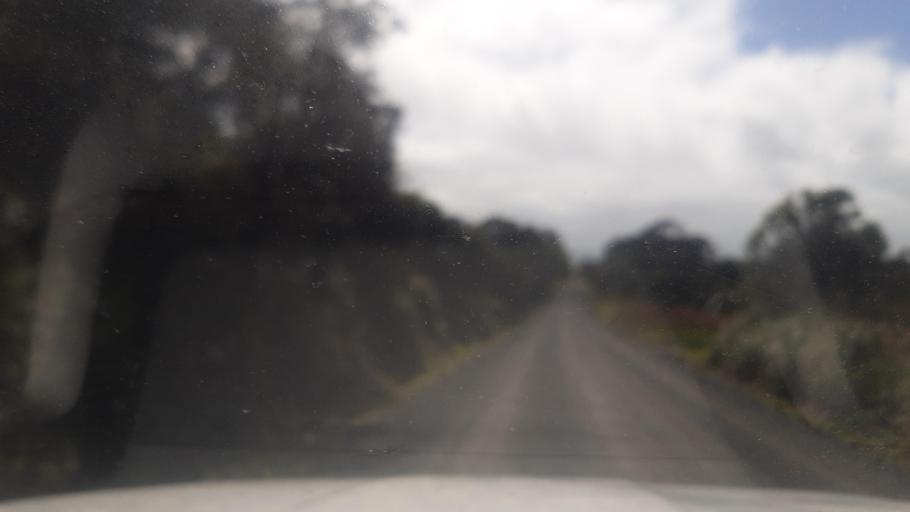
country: NZ
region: Northland
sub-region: Far North District
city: Kaitaia
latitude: -34.7435
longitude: 173.1055
